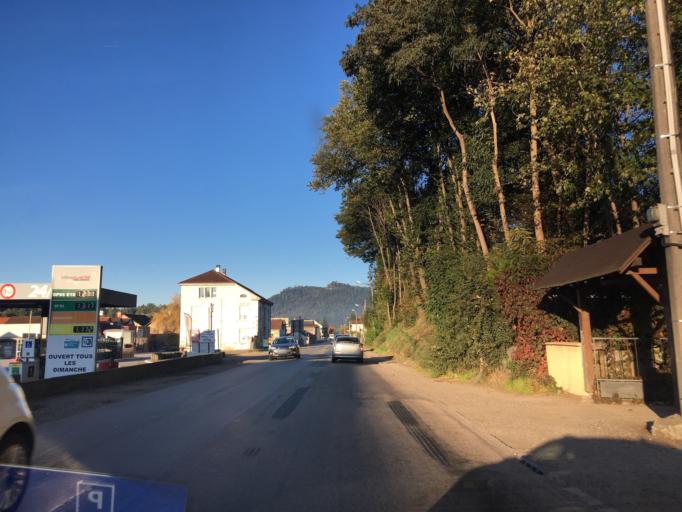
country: FR
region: Lorraine
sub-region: Departement des Vosges
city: Moyenmoutier
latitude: 48.3781
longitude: 6.8931
